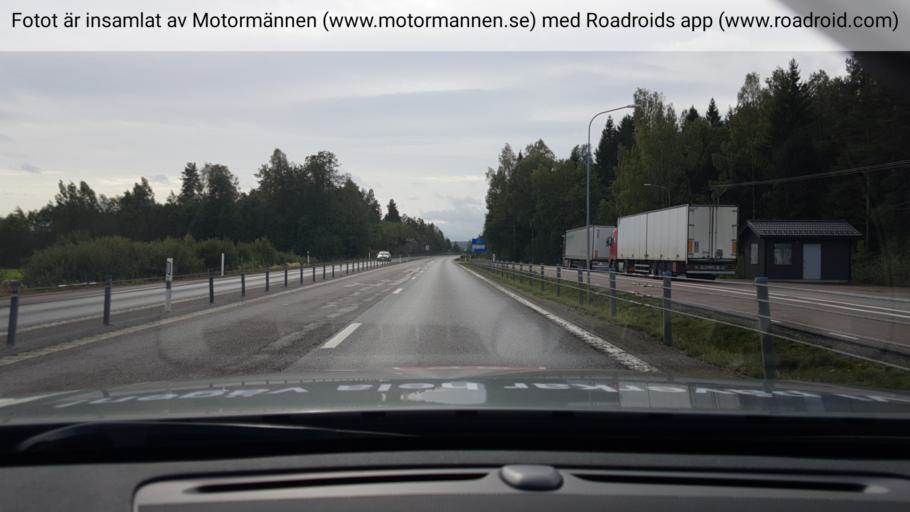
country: SE
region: Vaermland
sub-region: Grums Kommun
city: Grums
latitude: 59.3586
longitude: 13.1318
